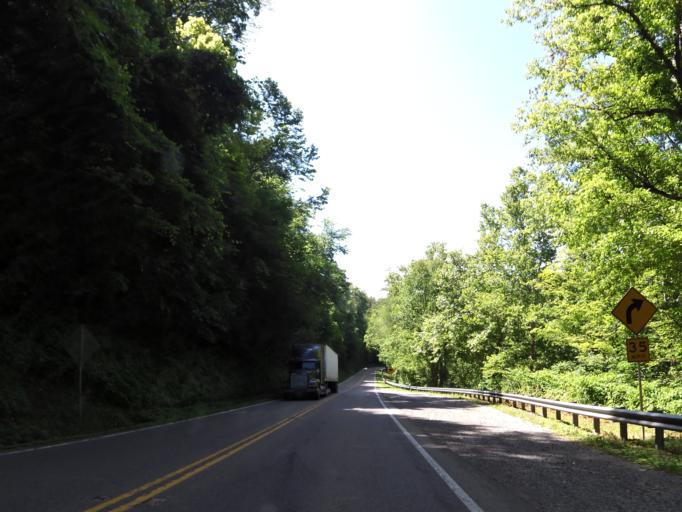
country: US
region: Virginia
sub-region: Lee County
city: Pennington Gap
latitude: 36.7493
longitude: -83.0089
